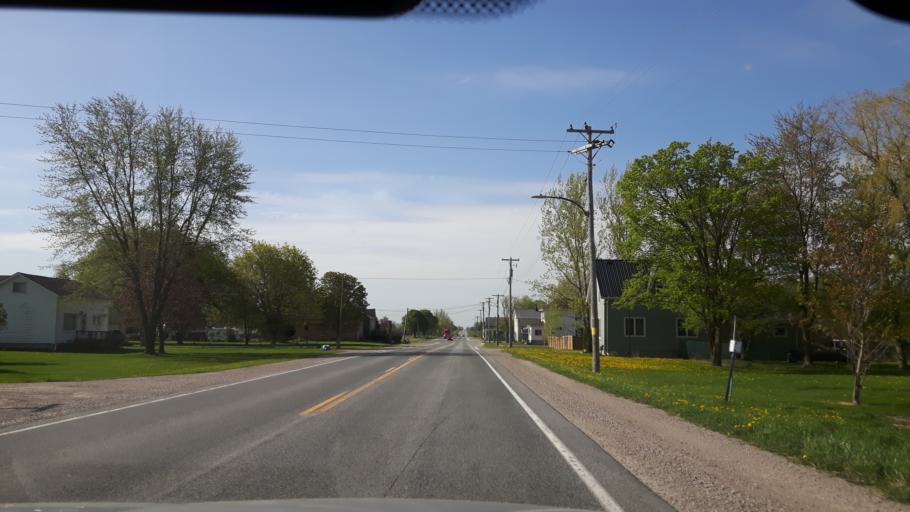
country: CA
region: Ontario
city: Bluewater
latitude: 43.4731
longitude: -81.5064
